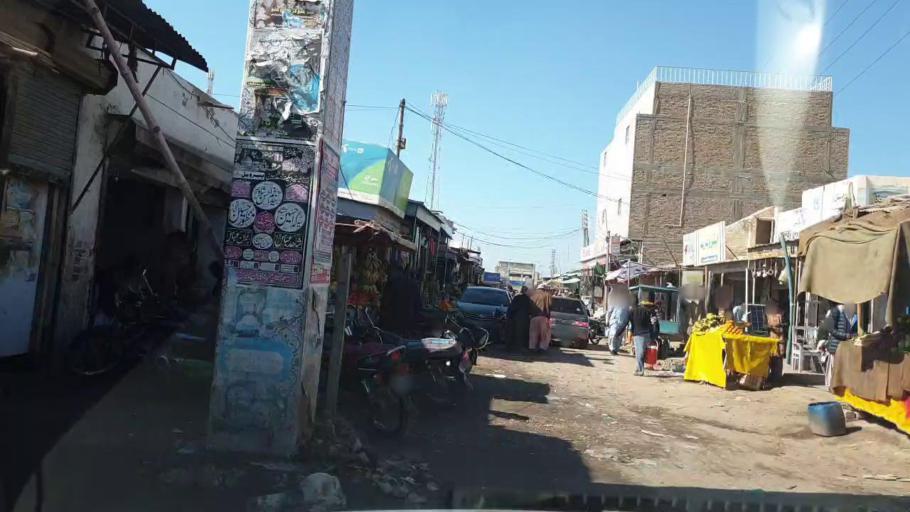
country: PK
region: Sindh
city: Tando Mittha Khan
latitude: 25.7963
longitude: 69.0716
